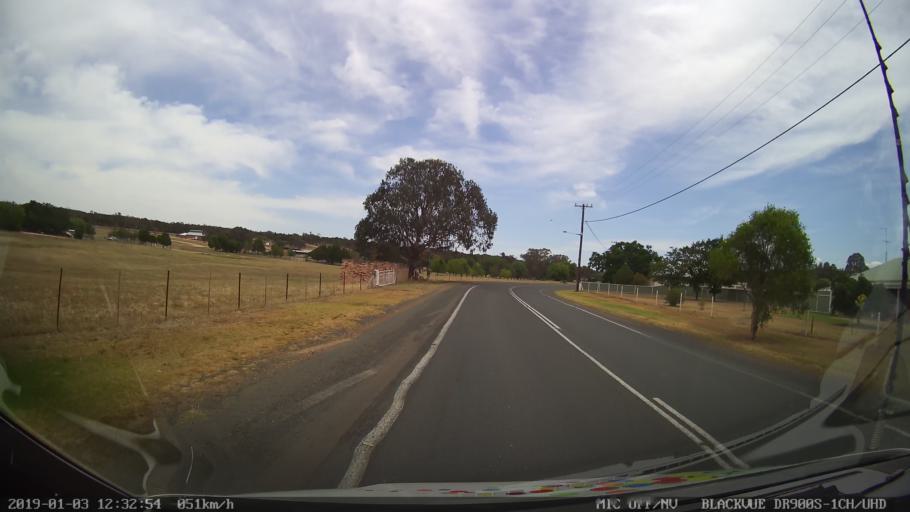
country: AU
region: New South Wales
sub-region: Weddin
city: Grenfell
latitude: -33.8894
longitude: 148.1621
